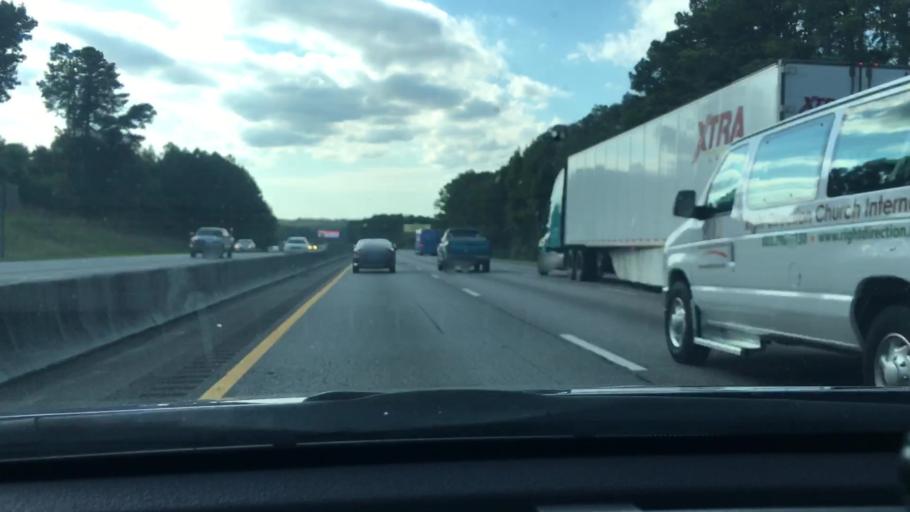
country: US
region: South Carolina
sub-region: Richland County
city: Forest Acres
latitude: 34.0664
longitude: -81.0340
